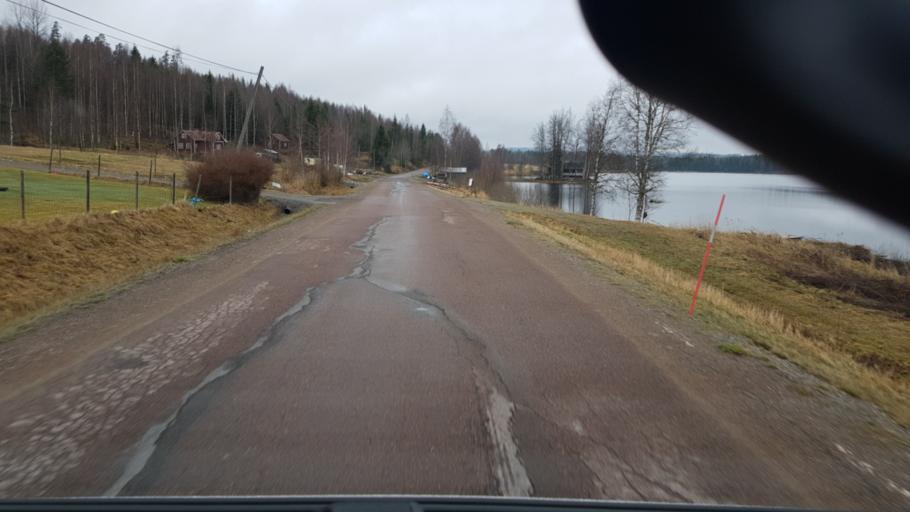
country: SE
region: Vaermland
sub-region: Eda Kommun
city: Charlottenberg
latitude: 59.9418
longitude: 12.5239
